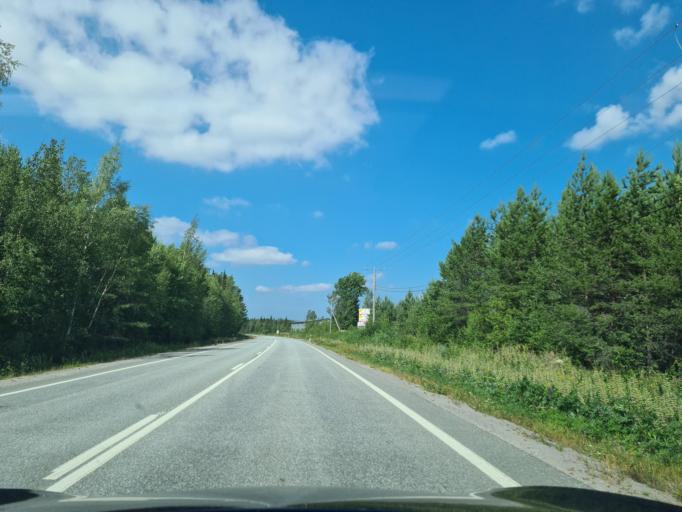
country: FI
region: Ostrobothnia
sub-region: Vaasa
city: Vaasa
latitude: 63.1660
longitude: 21.5892
